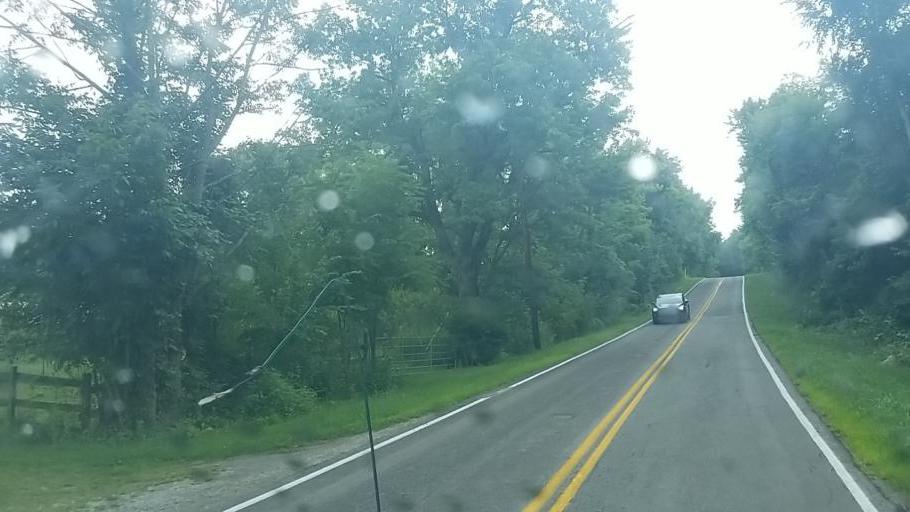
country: US
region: Ohio
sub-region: Lorain County
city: Lagrange
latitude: 41.1811
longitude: -82.0831
